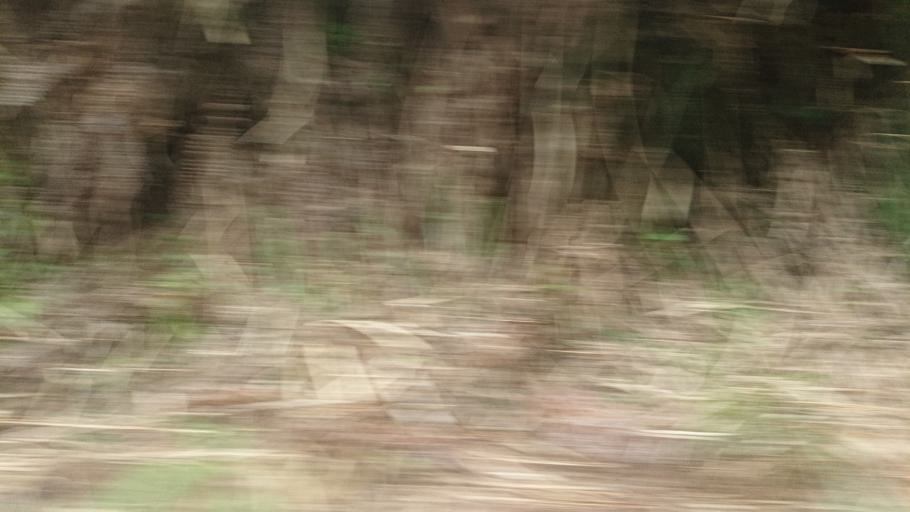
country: TW
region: Taiwan
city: Lugu
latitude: 23.6290
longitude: 120.7172
